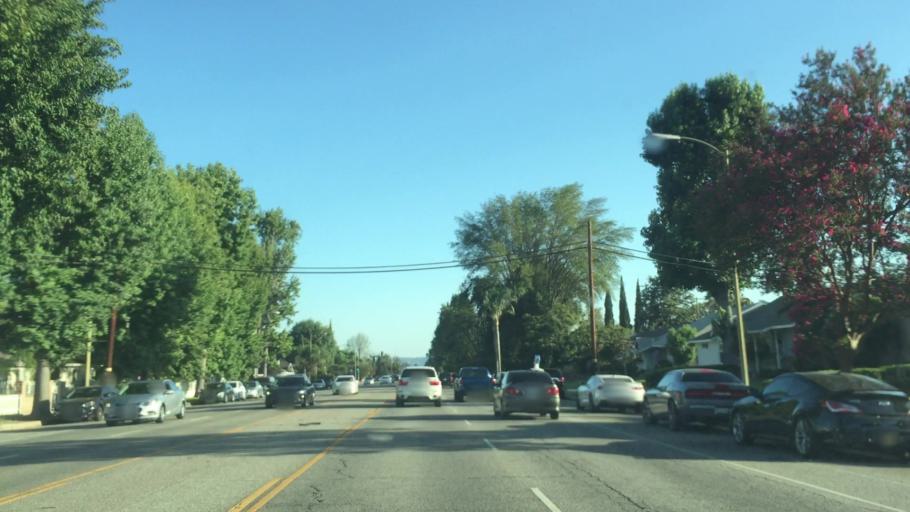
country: US
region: California
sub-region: Los Angeles County
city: Northridge
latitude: 34.2414
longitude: -118.4851
